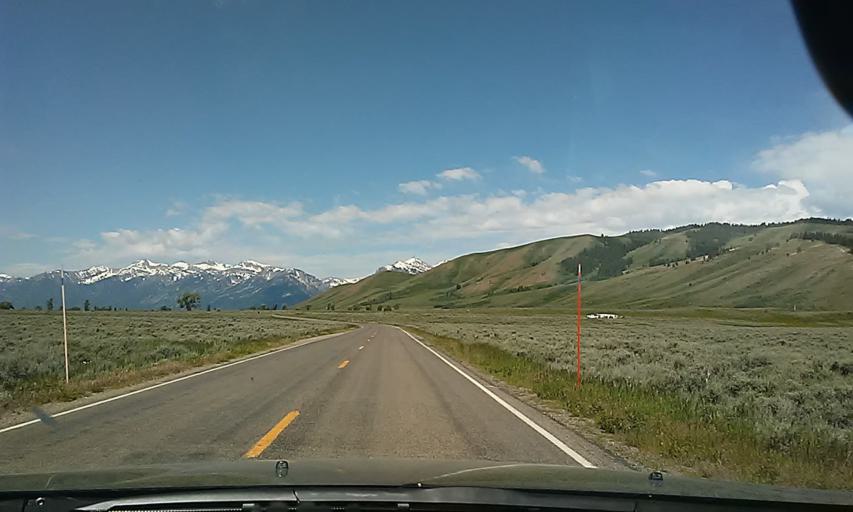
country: US
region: Wyoming
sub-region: Teton County
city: Jackson
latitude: 43.6252
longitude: -110.6593
